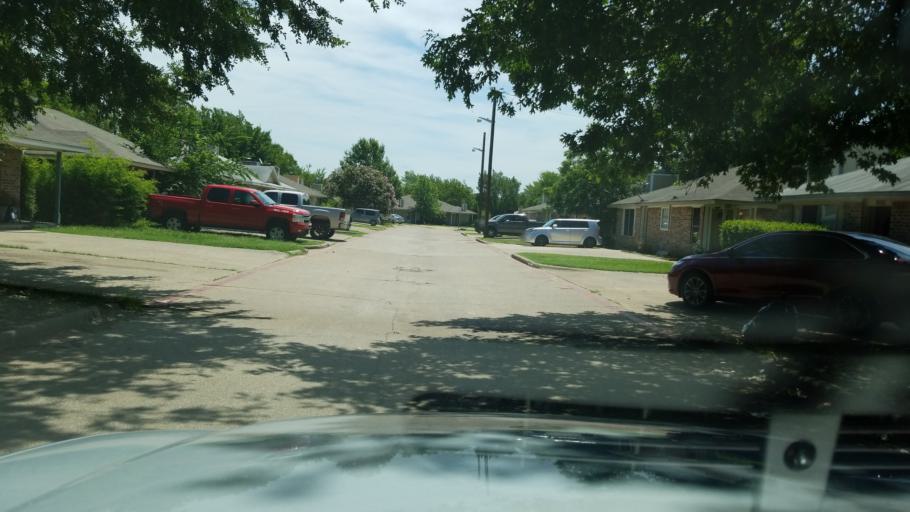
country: US
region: Texas
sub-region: Dallas County
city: Irving
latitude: 32.8046
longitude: -96.9241
